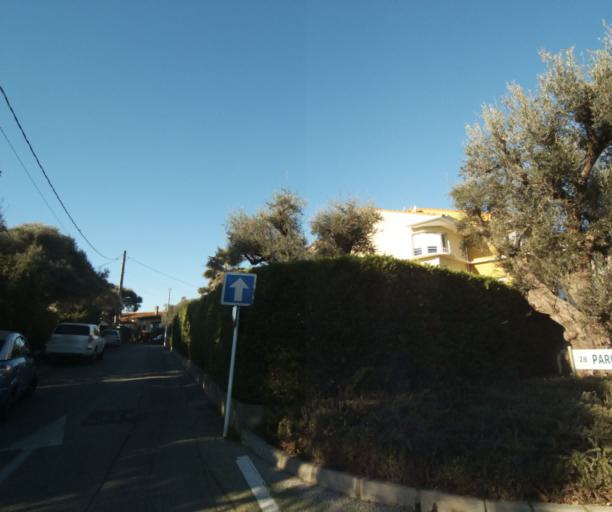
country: FR
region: Provence-Alpes-Cote d'Azur
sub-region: Departement des Alpes-Maritimes
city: Antibes
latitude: 43.5828
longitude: 7.1031
